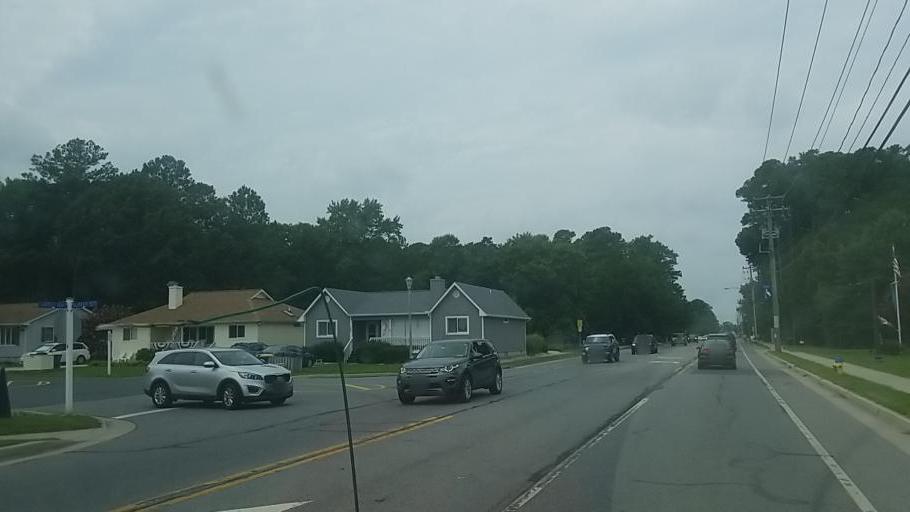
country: US
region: Delaware
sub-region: Sussex County
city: Ocean View
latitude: 38.5407
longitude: -75.0725
